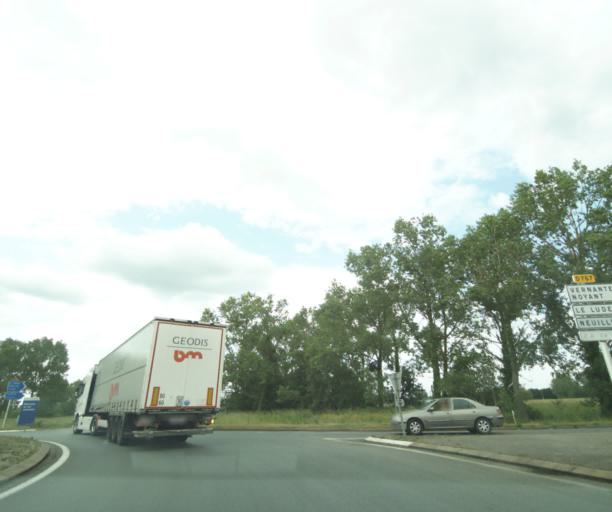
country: FR
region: Pays de la Loire
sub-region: Departement de Maine-et-Loire
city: Vivy
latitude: 47.3086
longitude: -0.0304
